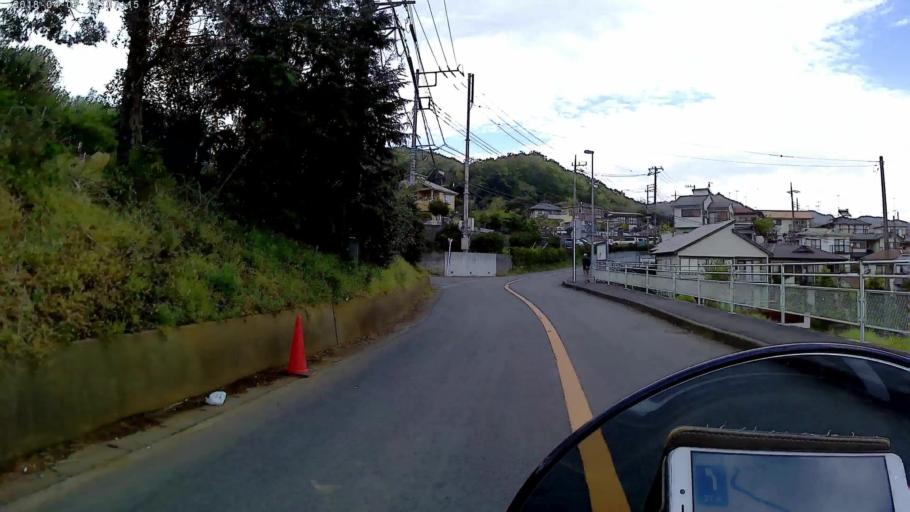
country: JP
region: Kanagawa
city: Hadano
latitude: 35.3646
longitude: 139.2520
